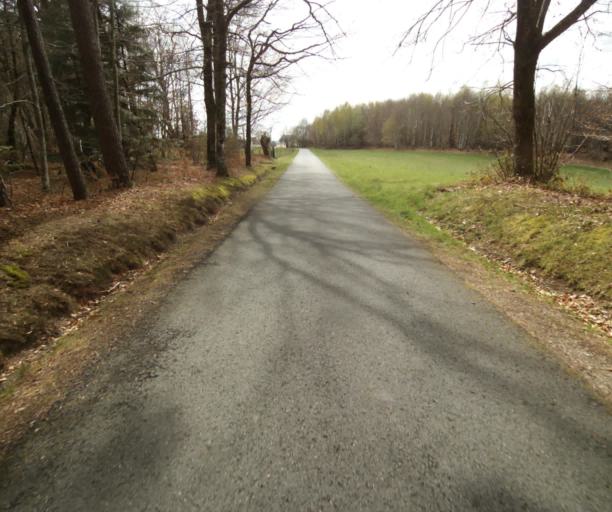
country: FR
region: Limousin
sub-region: Departement de la Correze
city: Laguenne
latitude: 45.2027
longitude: 1.8887
